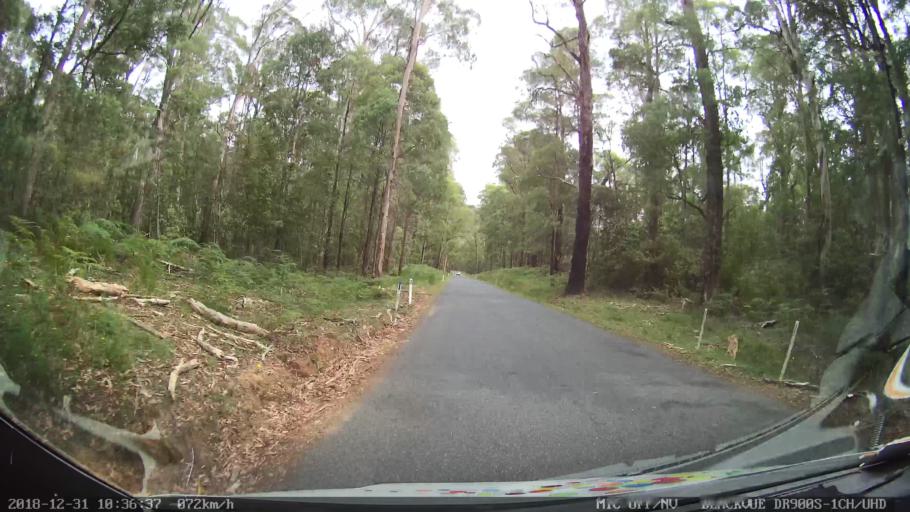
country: AU
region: New South Wales
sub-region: Snowy River
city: Jindabyne
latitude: -36.4244
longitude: 148.1714
